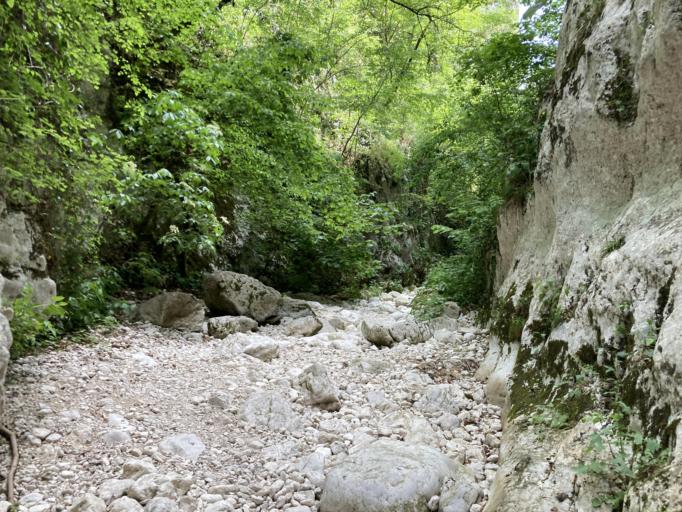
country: IT
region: Abruzzo
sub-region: Provincia dell' Aquila
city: Aielli
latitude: 42.1011
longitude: 13.5725
